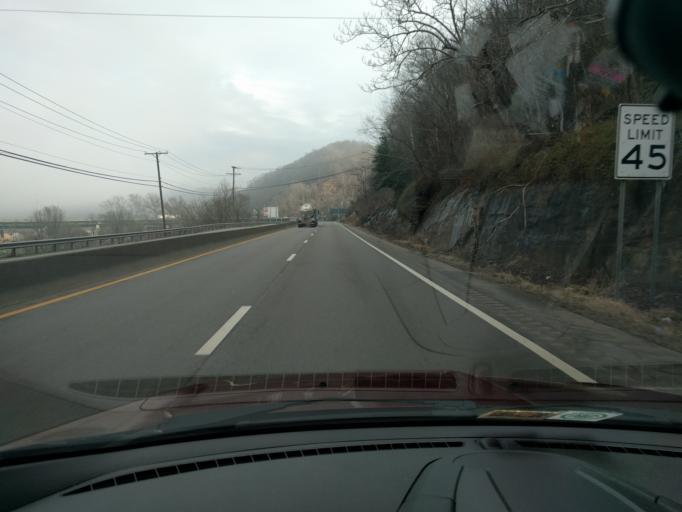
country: US
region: West Virginia
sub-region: Kanawha County
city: Rand
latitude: 38.3065
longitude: -81.5561
